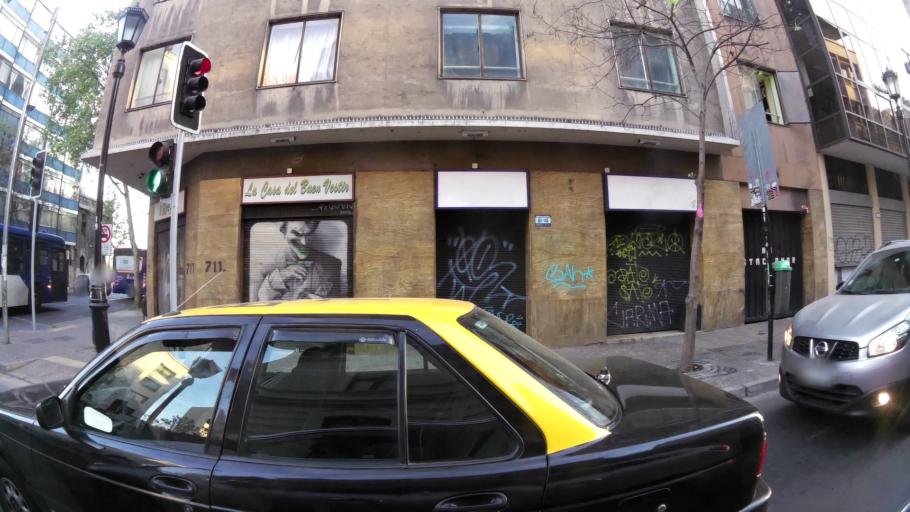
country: CL
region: Santiago Metropolitan
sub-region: Provincia de Santiago
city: Santiago
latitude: -33.4345
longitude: -70.6474
